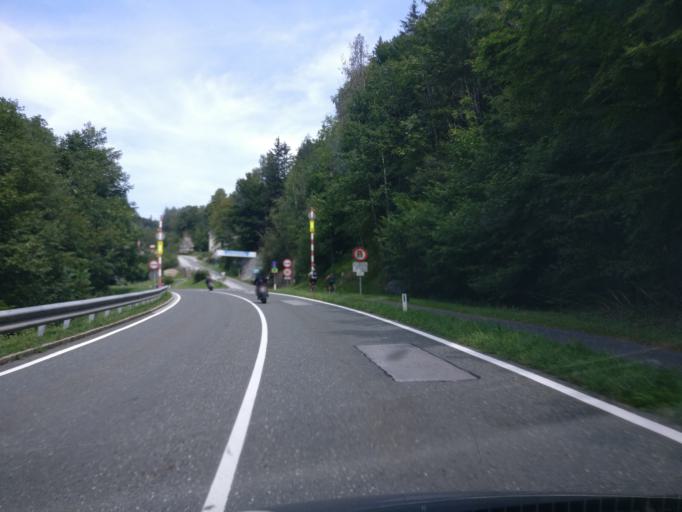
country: AT
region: Salzburg
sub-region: Politischer Bezirk Hallein
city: Scheffau am Tennengebirge
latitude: 47.5738
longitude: 13.1949
